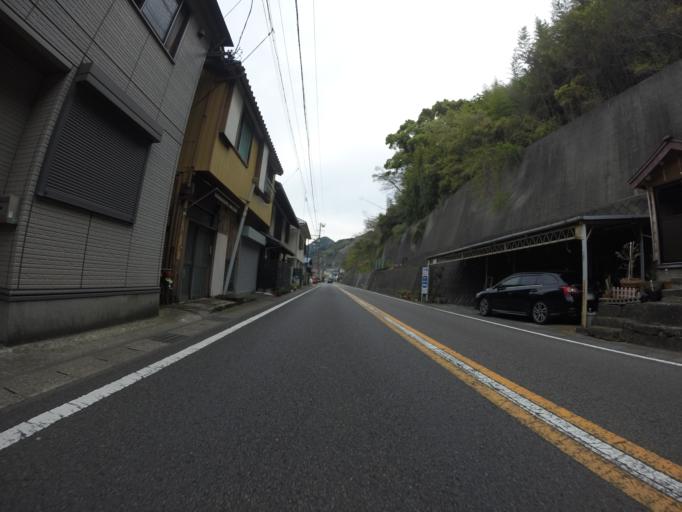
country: JP
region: Shizuoka
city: Fujinomiya
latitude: 35.0978
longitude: 138.5525
